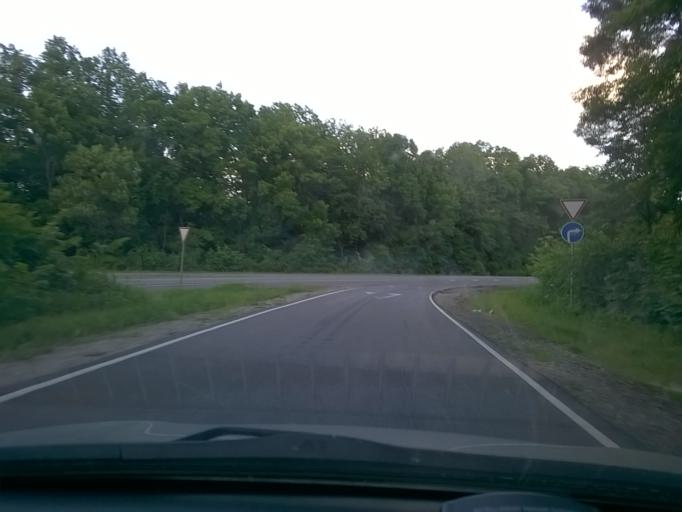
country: RU
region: Voronezj
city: Gribanovskiy
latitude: 51.4003
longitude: 42.0102
